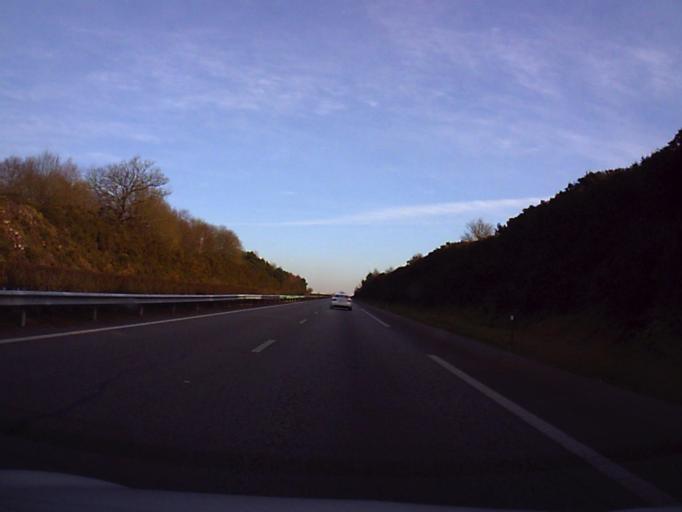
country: FR
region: Brittany
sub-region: Departement du Morbihan
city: Beignon
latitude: 47.9278
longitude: -2.1885
